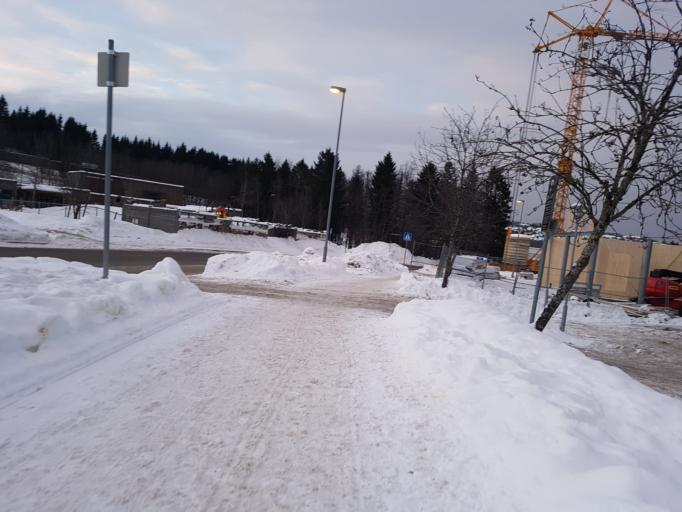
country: NO
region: Sor-Trondelag
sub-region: Trondheim
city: Trondheim
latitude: 63.3812
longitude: 10.3790
